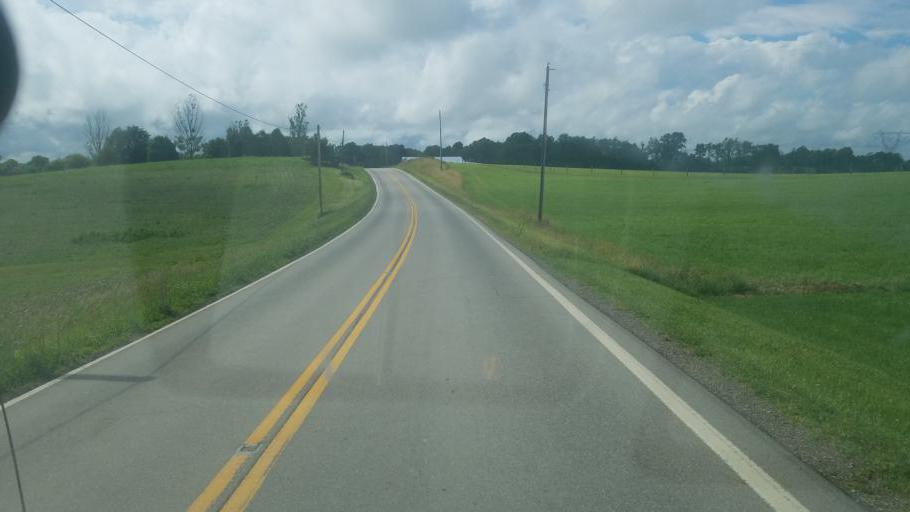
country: US
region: Ohio
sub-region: Carroll County
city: Carrollton
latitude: 40.4514
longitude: -80.9861
